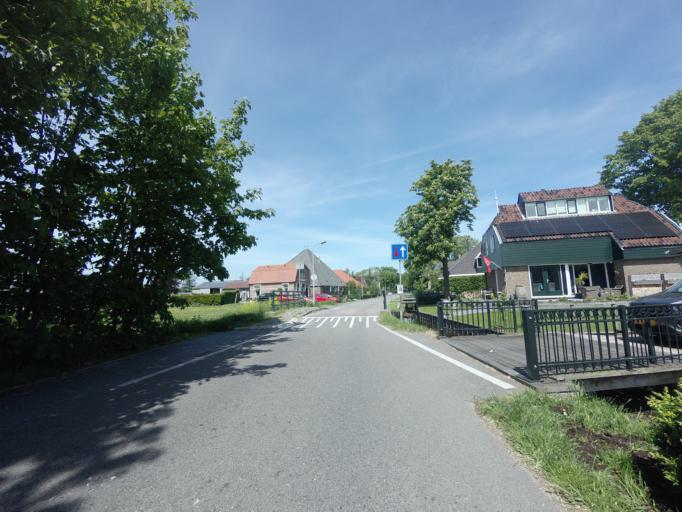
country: NL
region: North Holland
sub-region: Gemeente Velsen
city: Velsen-Zuid
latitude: 52.4419
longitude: 4.7181
